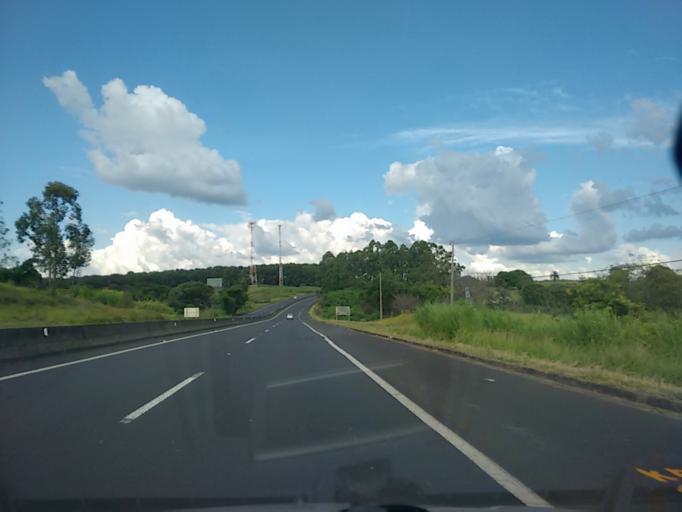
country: BR
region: Sao Paulo
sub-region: Marilia
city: Marilia
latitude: -22.2158
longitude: -49.8494
